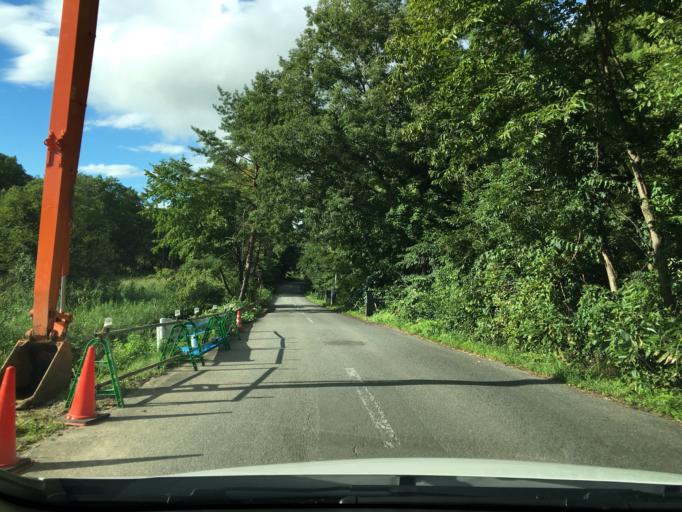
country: JP
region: Yamagata
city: Yonezawa
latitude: 37.9082
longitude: 140.2052
